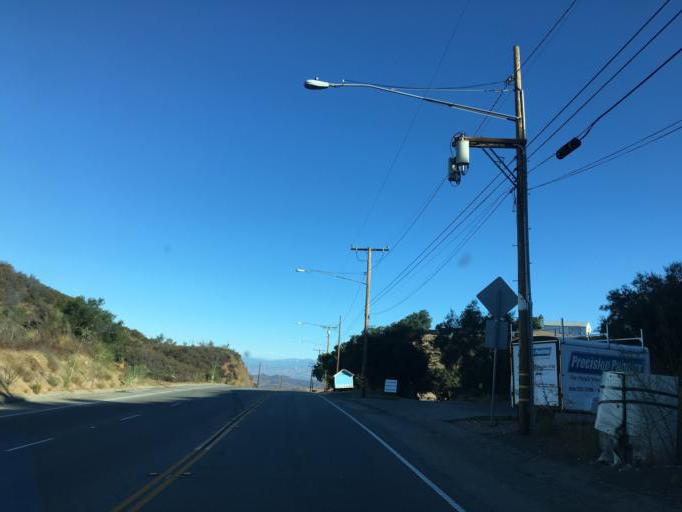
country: US
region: California
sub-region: Los Angeles County
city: Westlake Village
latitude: 34.1014
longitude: -118.8110
